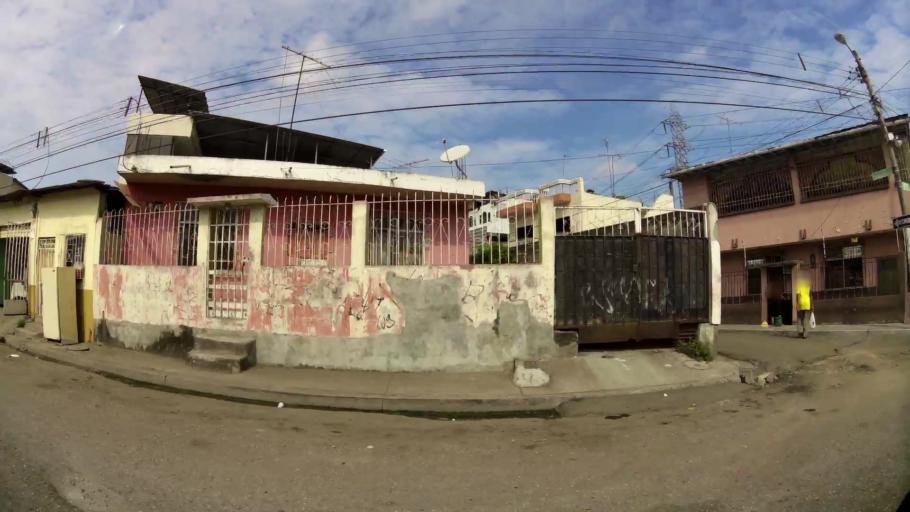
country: EC
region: Guayas
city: Guayaquil
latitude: -2.2587
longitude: -79.8939
